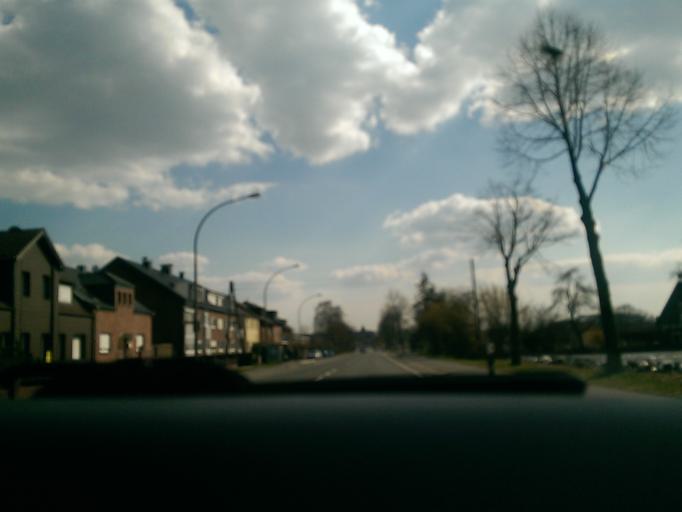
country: DE
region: North Rhine-Westphalia
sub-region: Regierungsbezirk Munster
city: Muenster
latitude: 51.9182
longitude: 7.6319
